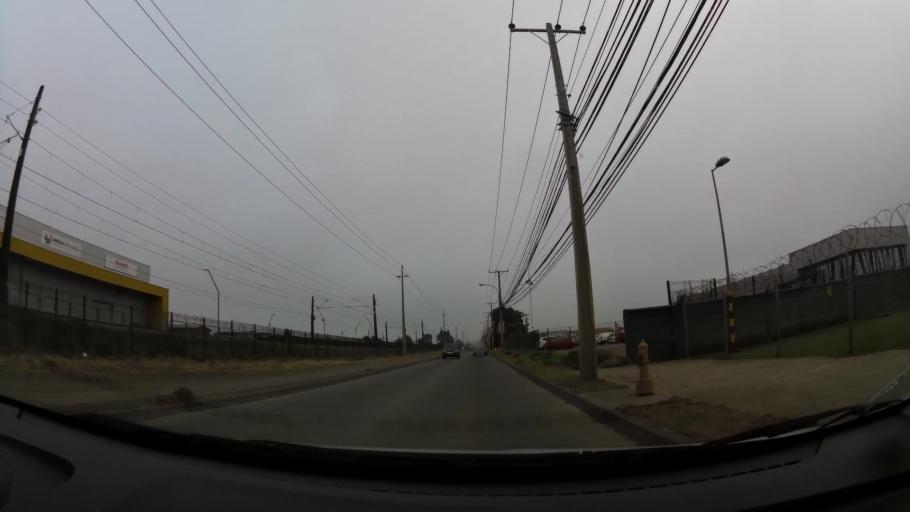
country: CL
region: Biobio
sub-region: Provincia de Concepcion
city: Concepcion
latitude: -36.8017
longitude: -73.0784
